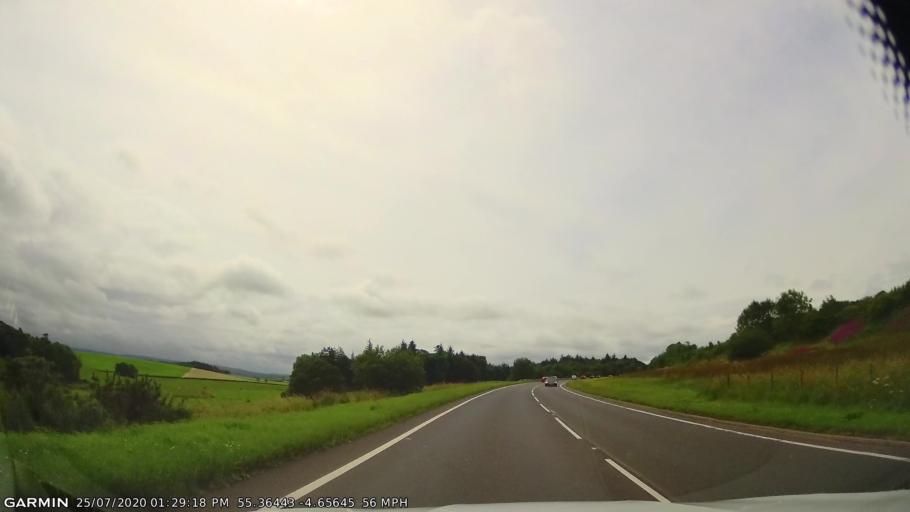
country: GB
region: Scotland
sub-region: South Ayrshire
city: Maybole
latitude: 55.3642
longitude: -4.6562
